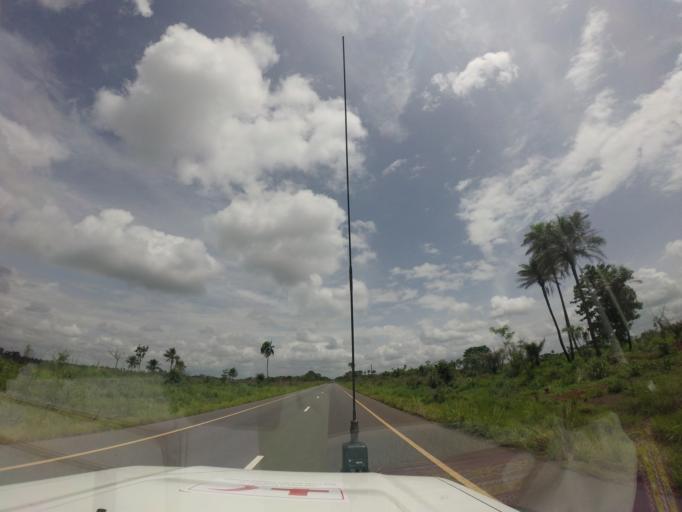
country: SL
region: Northern Province
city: Port Loko
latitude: 8.8067
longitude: -12.7553
